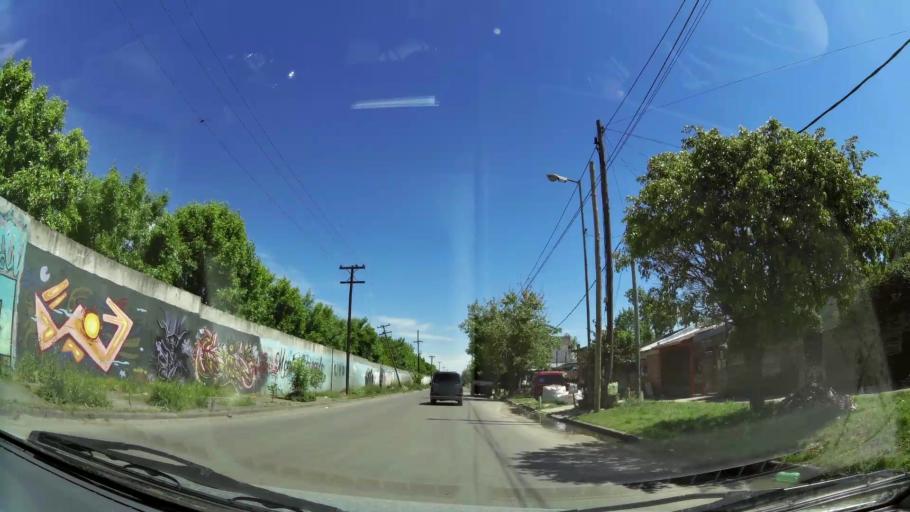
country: AR
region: Buenos Aires
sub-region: Partido de Lanus
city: Lanus
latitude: -34.7296
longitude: -58.3363
